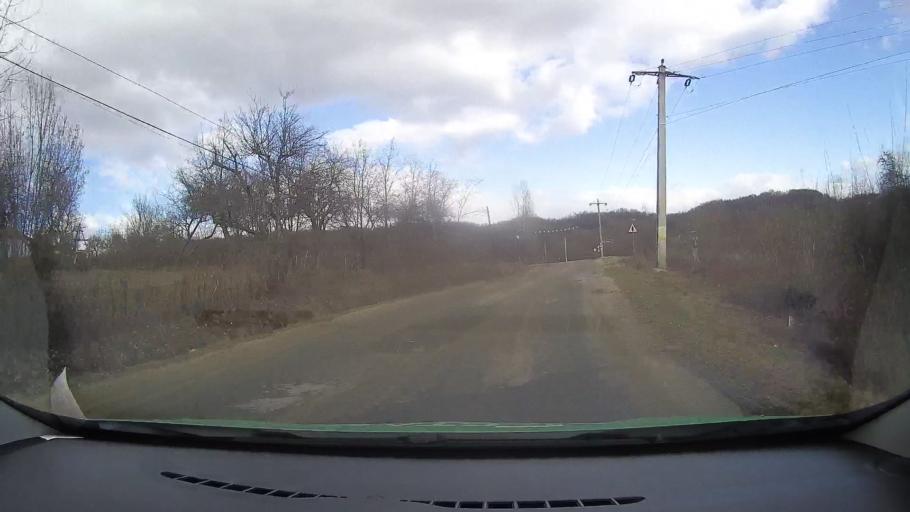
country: RO
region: Dambovita
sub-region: Comuna Buciumeni
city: Buciumeni
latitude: 45.1341
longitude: 25.4672
